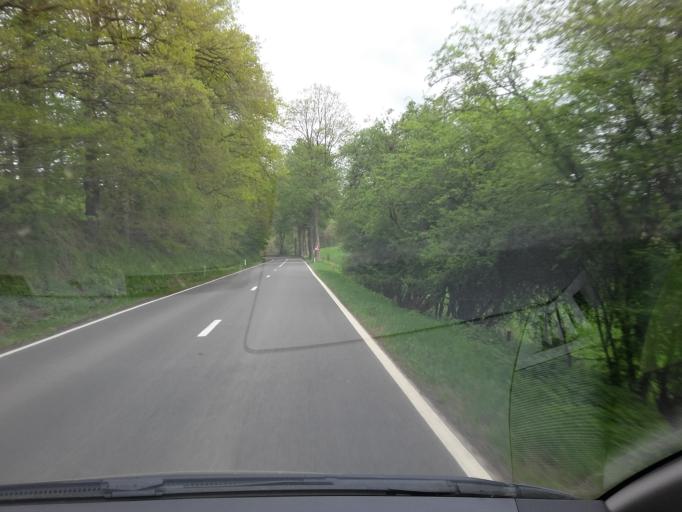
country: BE
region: Wallonia
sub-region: Province du Luxembourg
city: Neufchateau
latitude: 49.8281
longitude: 5.4175
